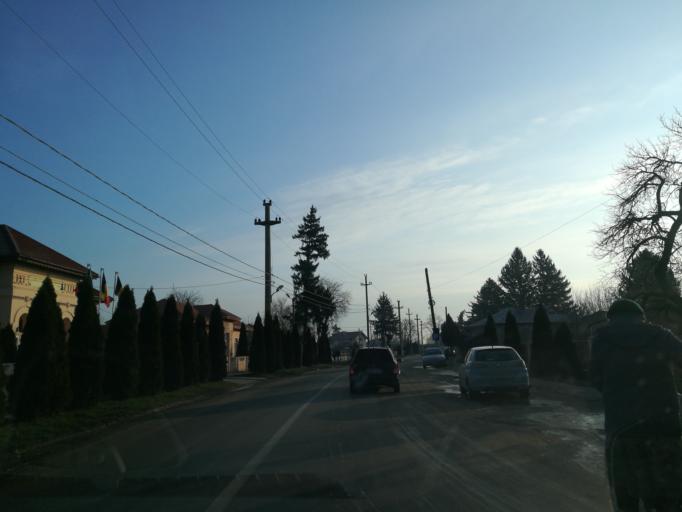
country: RO
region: Ialomita
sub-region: Comuna Fierbinti-Targ
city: Fierbintii de Jos
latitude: 44.6822
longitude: 26.3790
